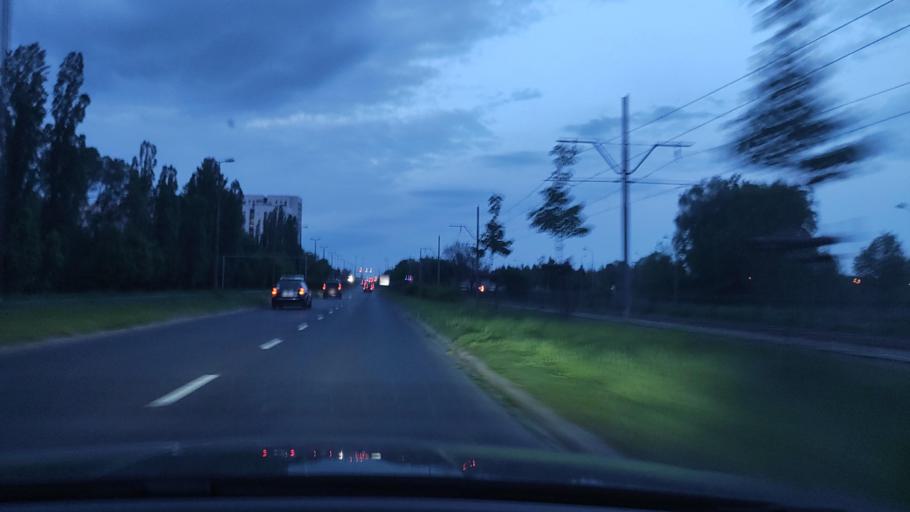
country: PL
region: Greater Poland Voivodeship
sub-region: Poznan
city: Poznan
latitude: 52.4098
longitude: 16.9735
